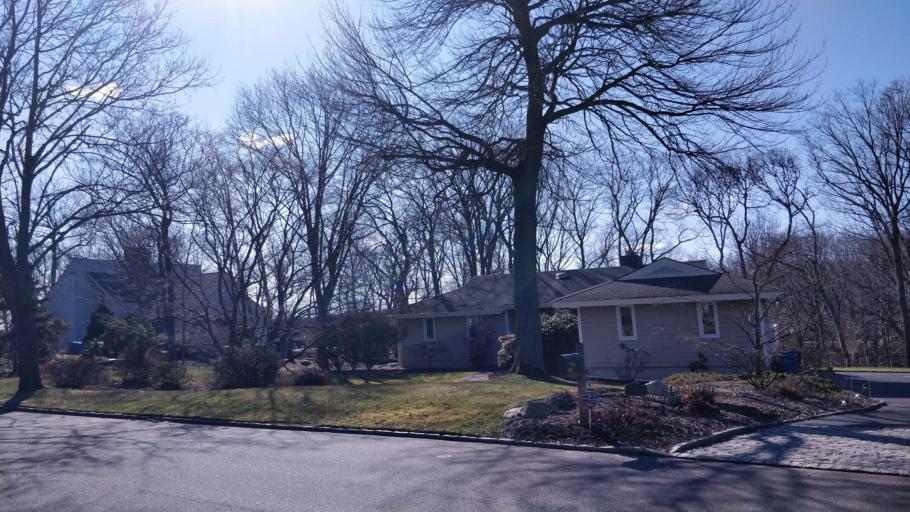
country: US
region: New York
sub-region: Suffolk County
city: Mount Sinai
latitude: 40.9599
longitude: -73.0458
